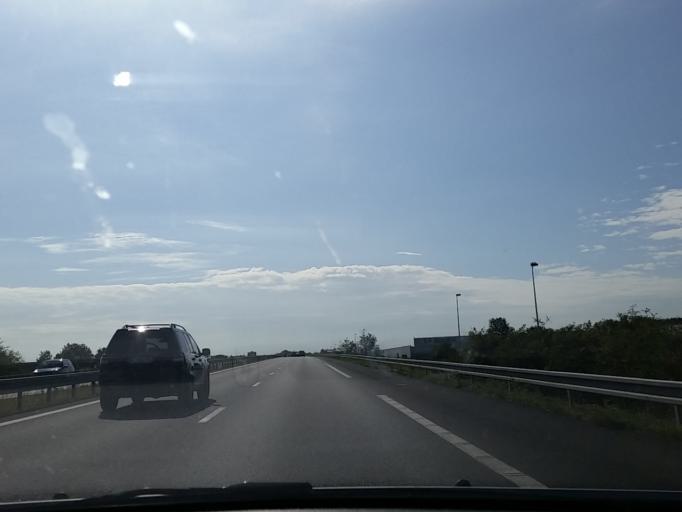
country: FR
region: Centre
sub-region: Departement du Cher
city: La Chapelle-Saint-Ursin
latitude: 47.0503
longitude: 2.3217
